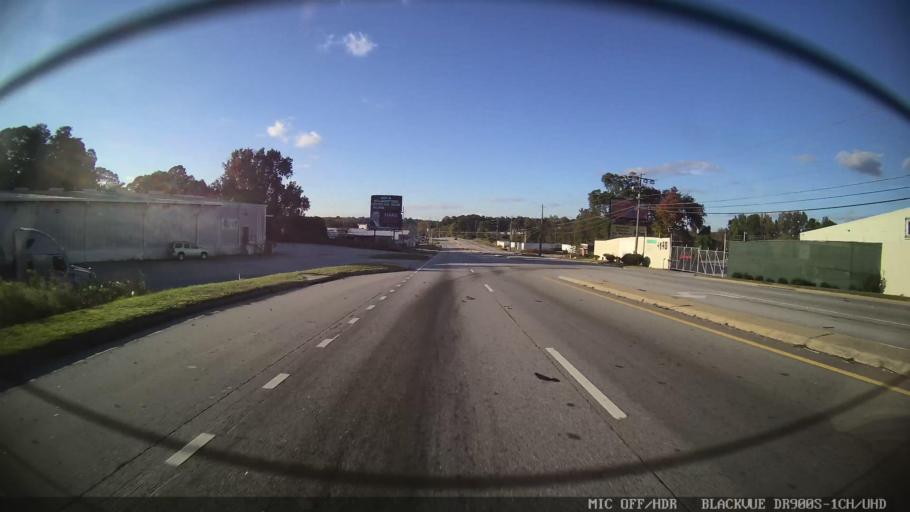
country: US
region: Georgia
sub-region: Clayton County
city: Conley
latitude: 33.6413
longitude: -84.3228
